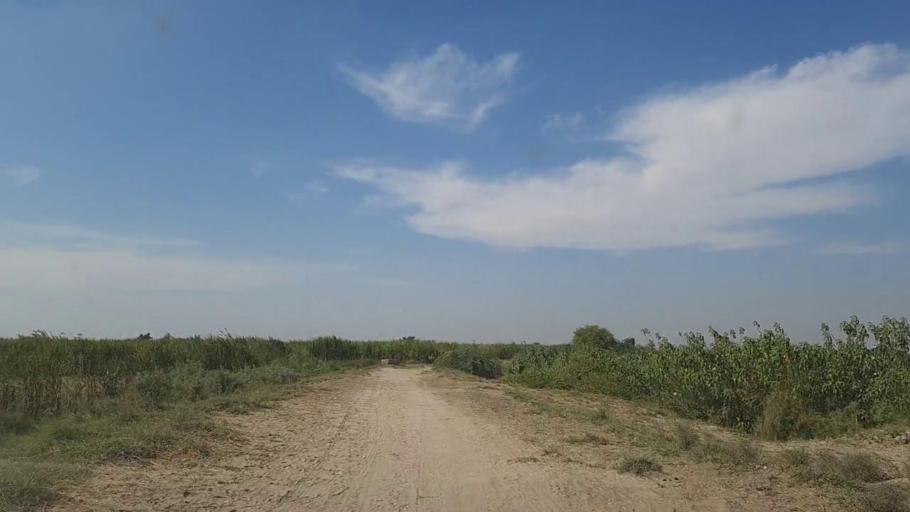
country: PK
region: Sindh
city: Mirpur Batoro
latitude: 24.8074
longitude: 68.2661
